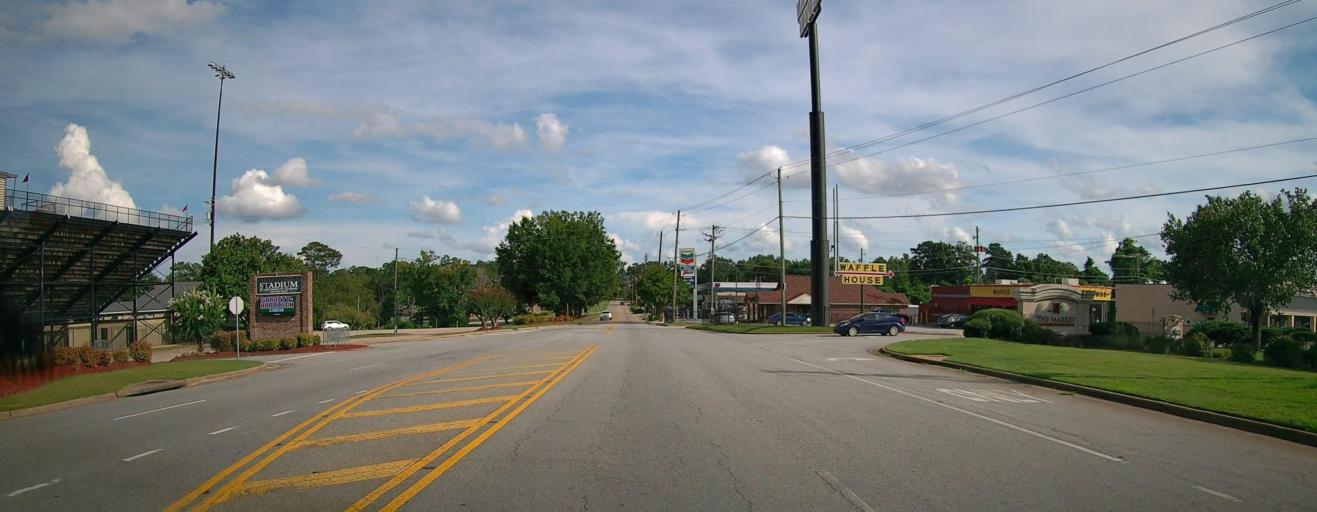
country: US
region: Alabama
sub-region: Russell County
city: Phenix City
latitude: 32.4979
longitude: -85.0164
